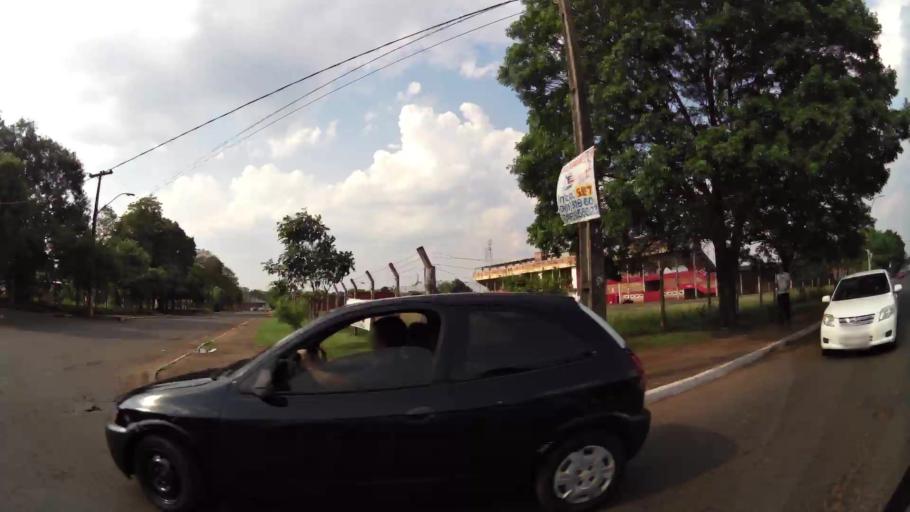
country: PY
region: Alto Parana
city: Presidente Franco
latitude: -25.5283
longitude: -54.6137
